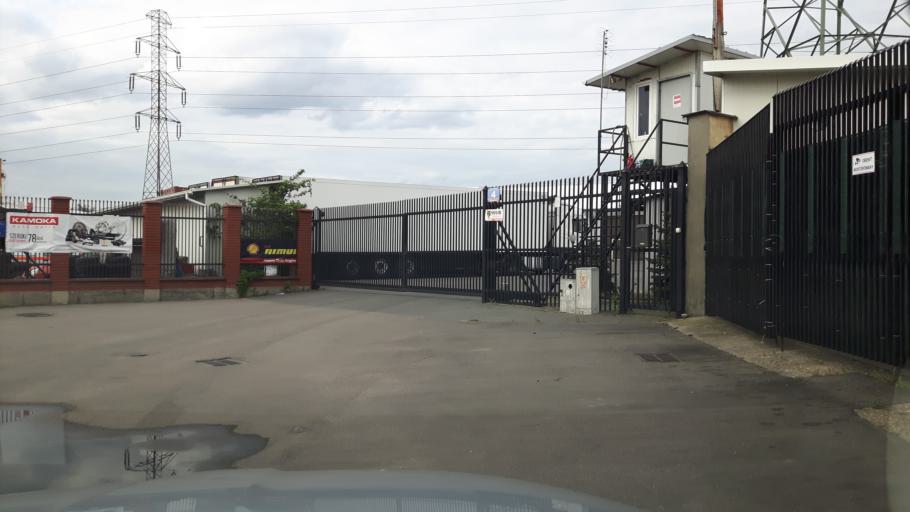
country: PL
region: Masovian Voivodeship
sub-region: Powiat wolominski
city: Zabki
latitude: 52.2883
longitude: 21.0901
